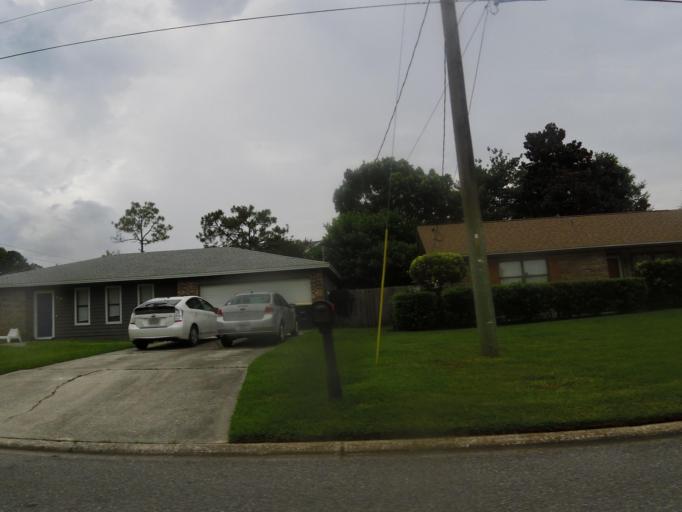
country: US
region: Florida
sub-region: Duval County
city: Jacksonville Beach
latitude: 30.2751
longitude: -81.4370
